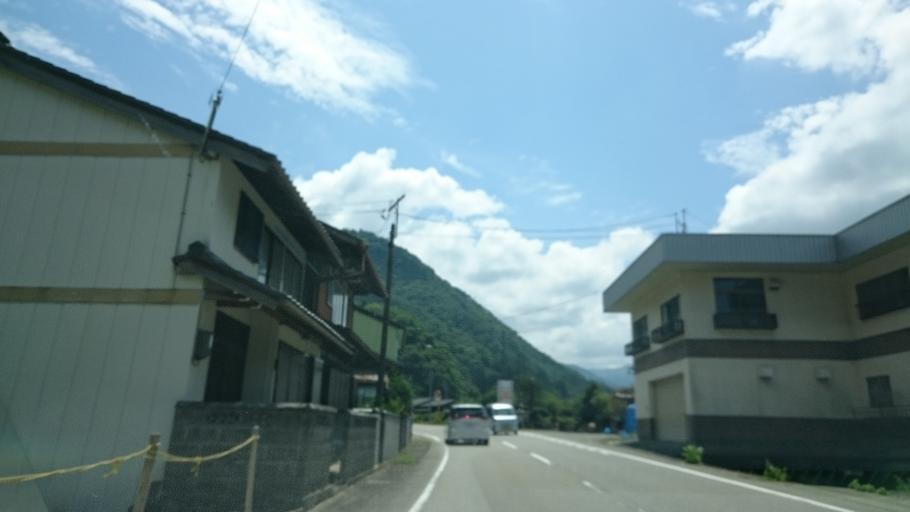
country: JP
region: Gifu
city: Takayama
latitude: 35.9268
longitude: 137.3073
